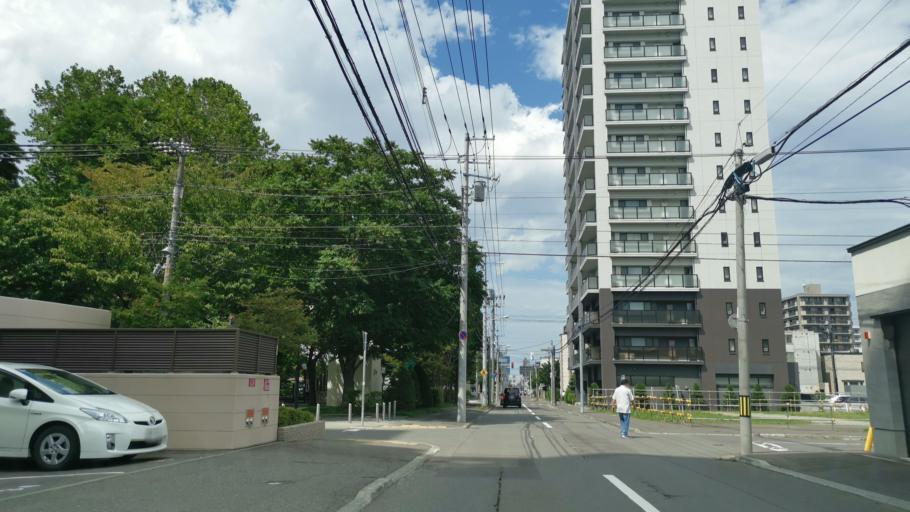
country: JP
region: Hokkaido
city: Sapporo
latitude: 43.0400
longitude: 141.3452
